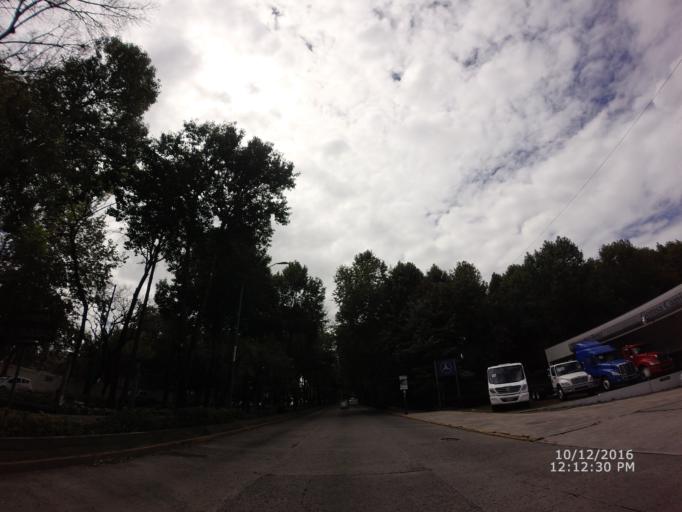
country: MX
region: Veracruz
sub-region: Xalapa
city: Xalapa de Enriquez
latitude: 19.5580
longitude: -96.9288
